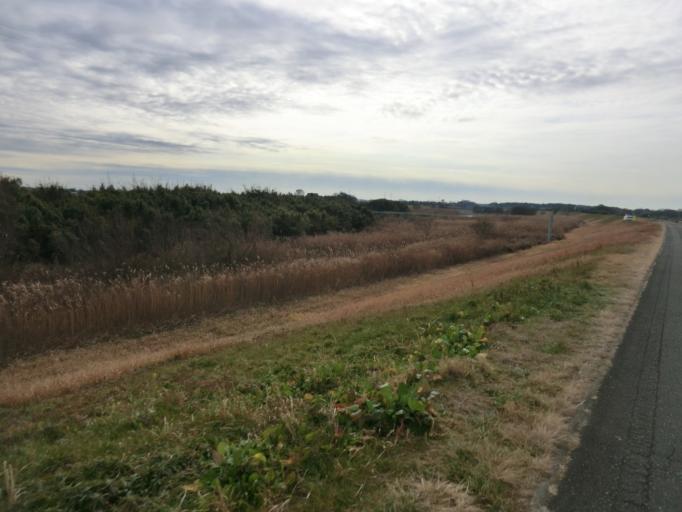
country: JP
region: Ibaraki
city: Mitsukaido
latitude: 36.0047
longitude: 139.9931
